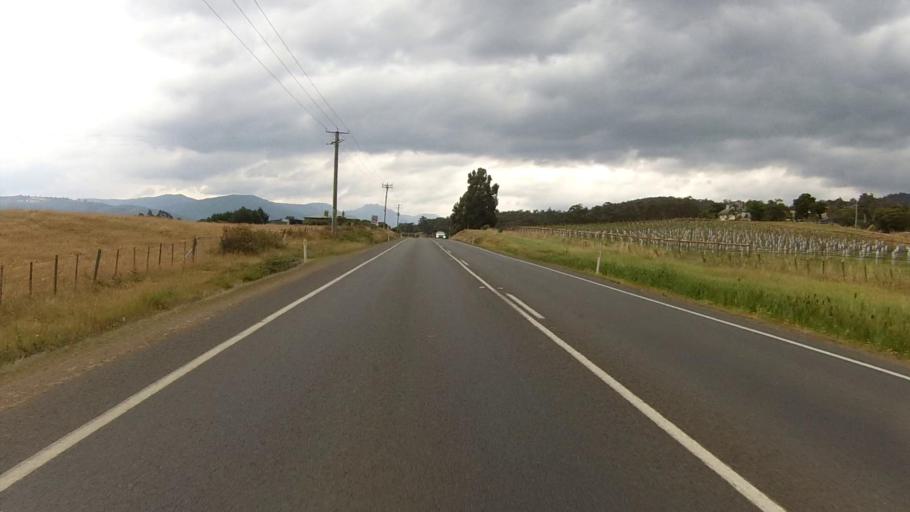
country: AU
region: Tasmania
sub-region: Huon Valley
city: Huonville
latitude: -43.0119
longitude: 147.0639
